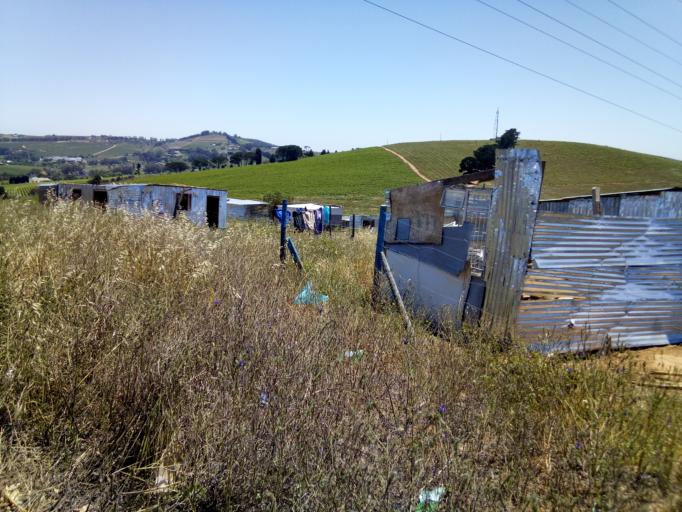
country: ZA
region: Western Cape
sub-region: Cape Winelands District Municipality
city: Stellenbosch
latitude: -33.9217
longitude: 18.8345
